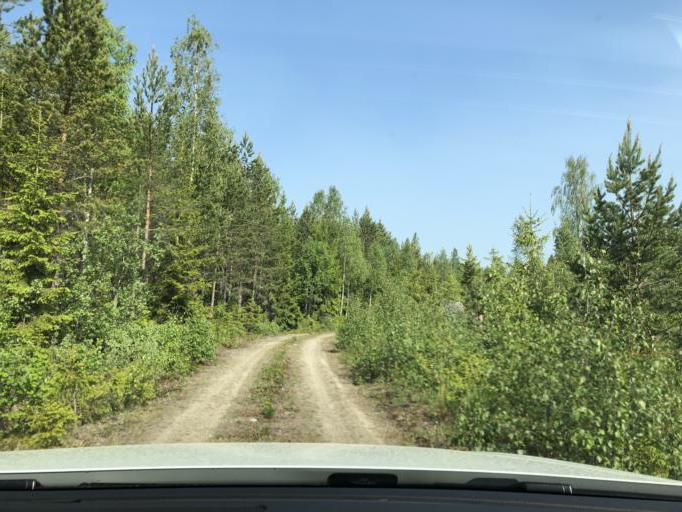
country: SE
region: Dalarna
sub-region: Avesta Kommun
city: Horndal
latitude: 60.2181
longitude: 16.5179
